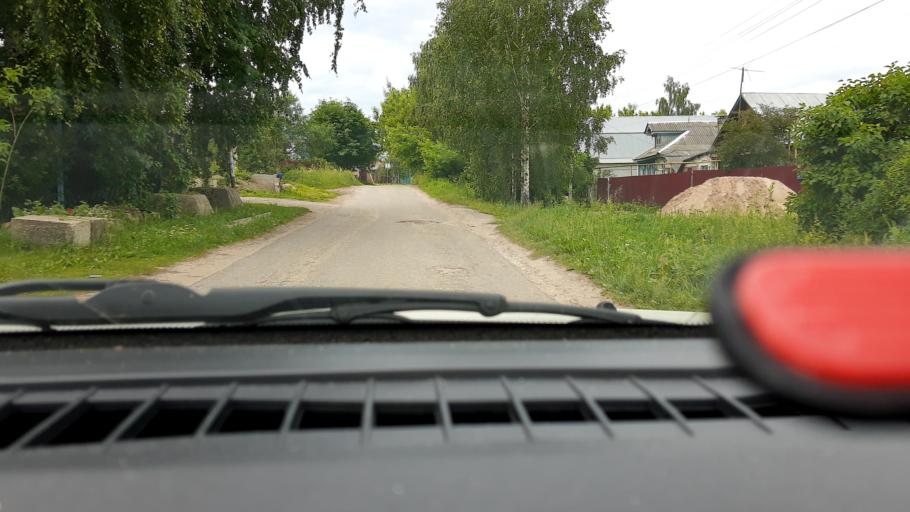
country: RU
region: Nizjnij Novgorod
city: Afonino
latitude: 56.2028
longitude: 44.1110
